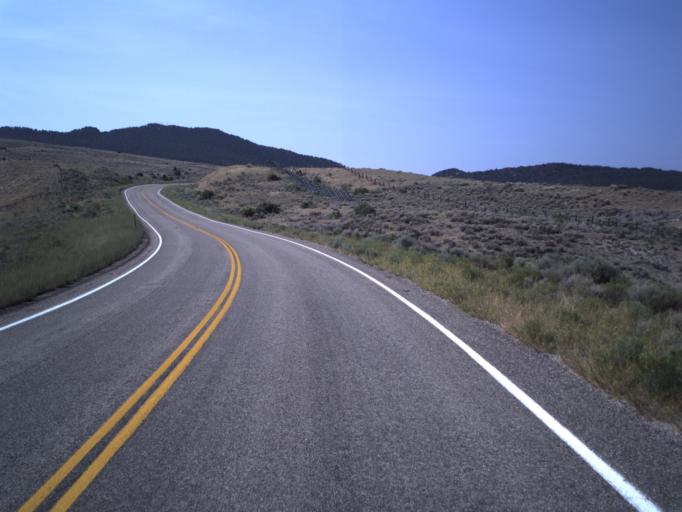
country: US
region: Utah
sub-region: Daggett County
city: Manila
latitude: 40.9739
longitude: -109.4635
